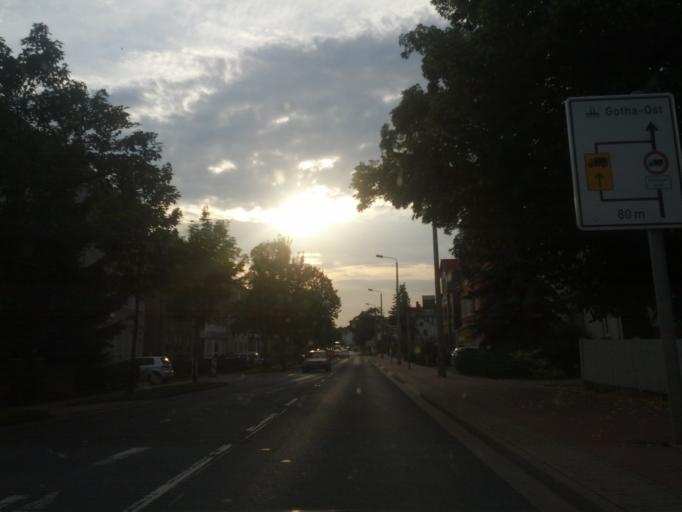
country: DE
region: Thuringia
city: Gotha
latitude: 50.9437
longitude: 10.7409
